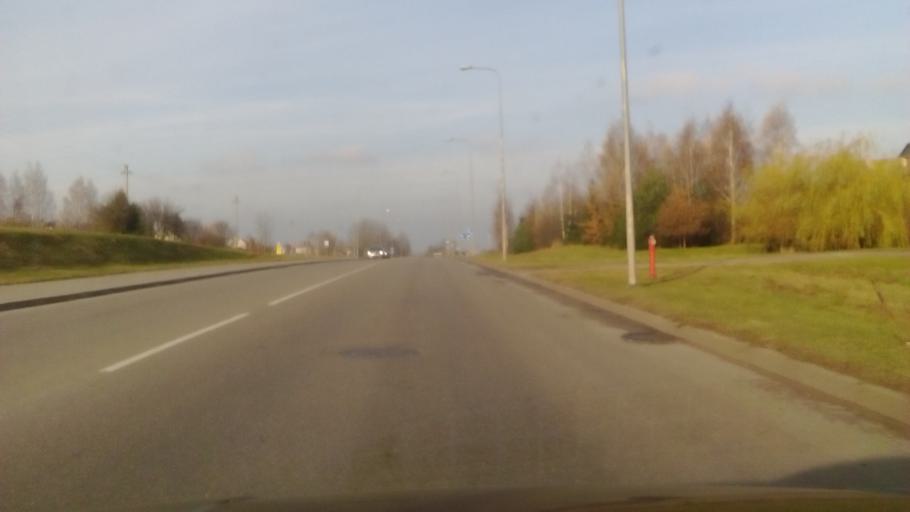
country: LT
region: Alytaus apskritis
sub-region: Alytus
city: Alytus
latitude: 54.3951
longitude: 23.9992
